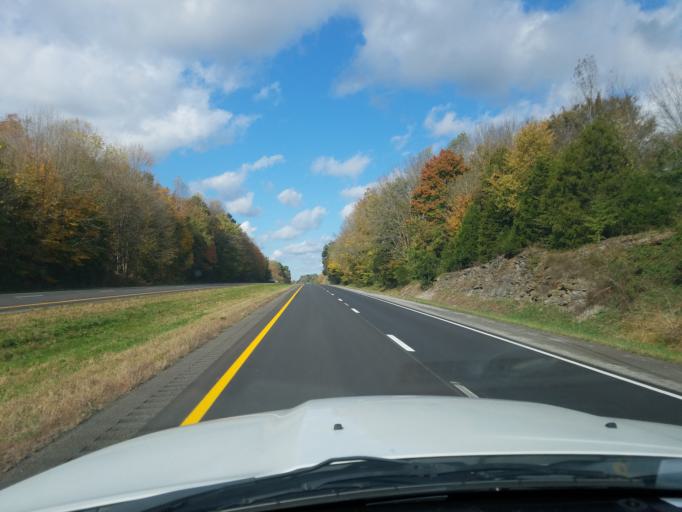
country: US
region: Kentucky
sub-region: Adair County
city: Columbia
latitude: 37.0827
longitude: -85.2509
